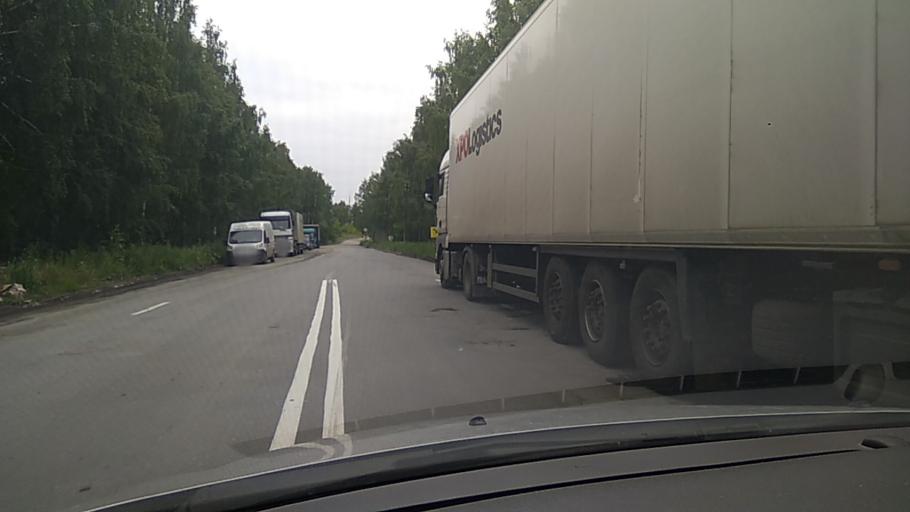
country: RU
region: Sverdlovsk
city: Shuvakish
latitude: 56.8912
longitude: 60.5185
